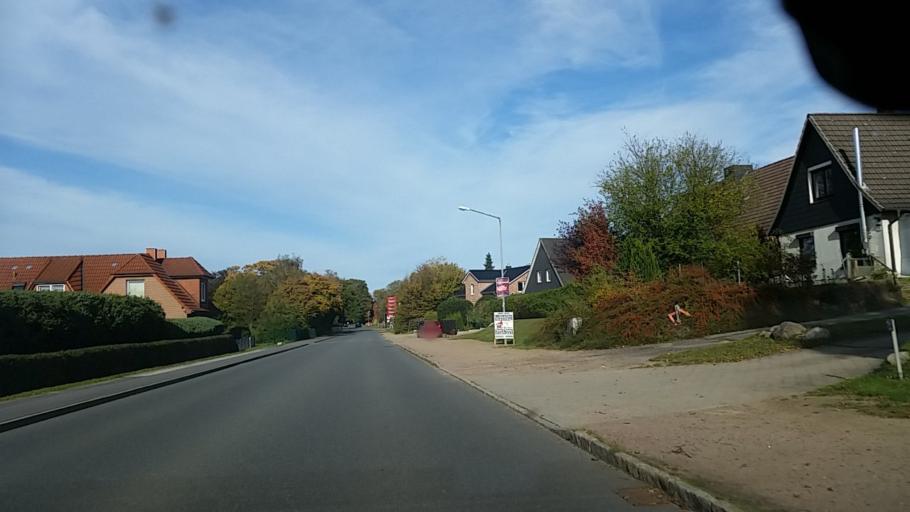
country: DE
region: Schleswig-Holstein
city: Delingsdorf
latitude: 53.7037
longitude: 10.2502
